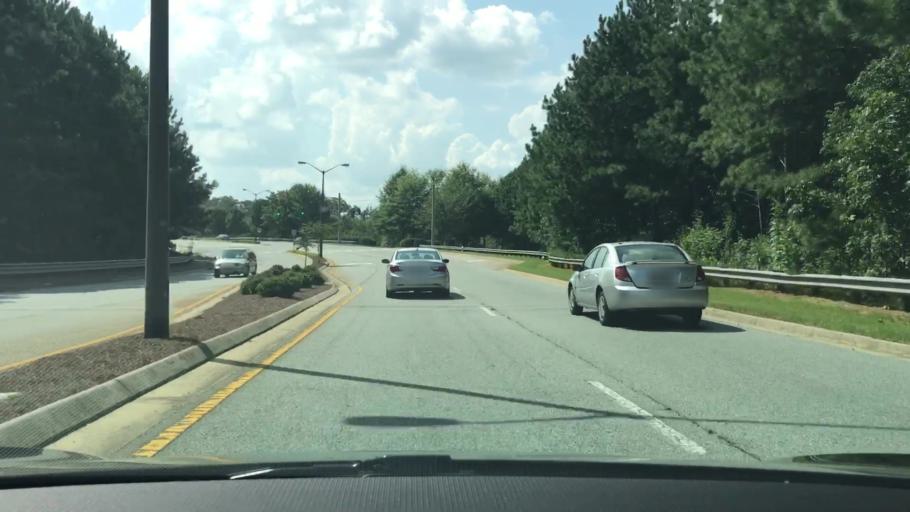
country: US
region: Georgia
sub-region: Gwinnett County
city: Suwanee
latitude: 34.0391
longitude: -84.0470
